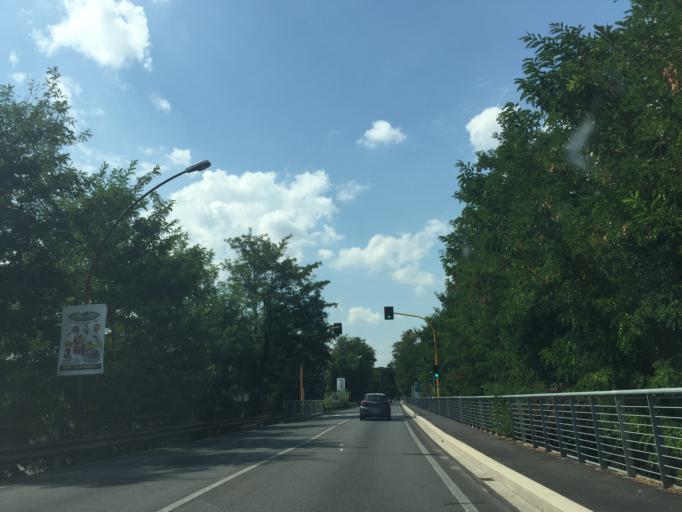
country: IT
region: Tuscany
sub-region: Province of Florence
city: San Mauro
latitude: 43.8033
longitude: 11.1292
